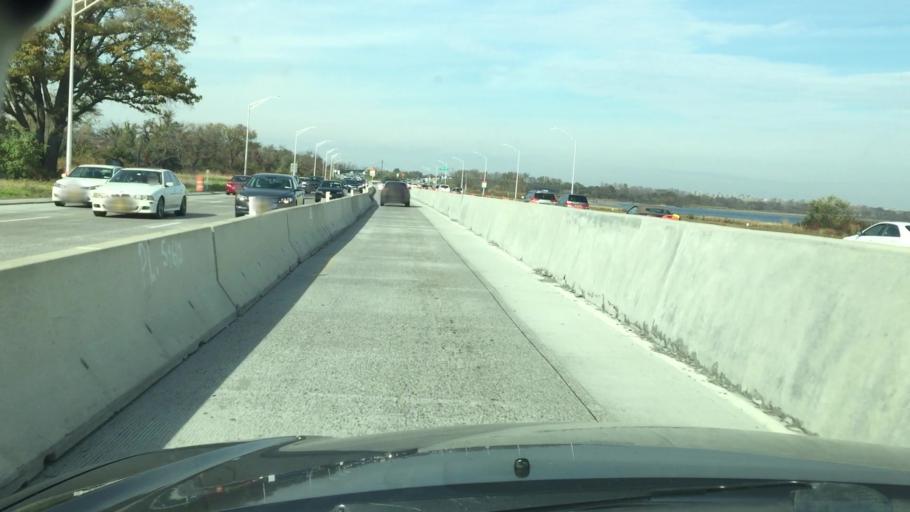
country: US
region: New York
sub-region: Kings County
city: East New York
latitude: 40.6142
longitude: -73.8971
